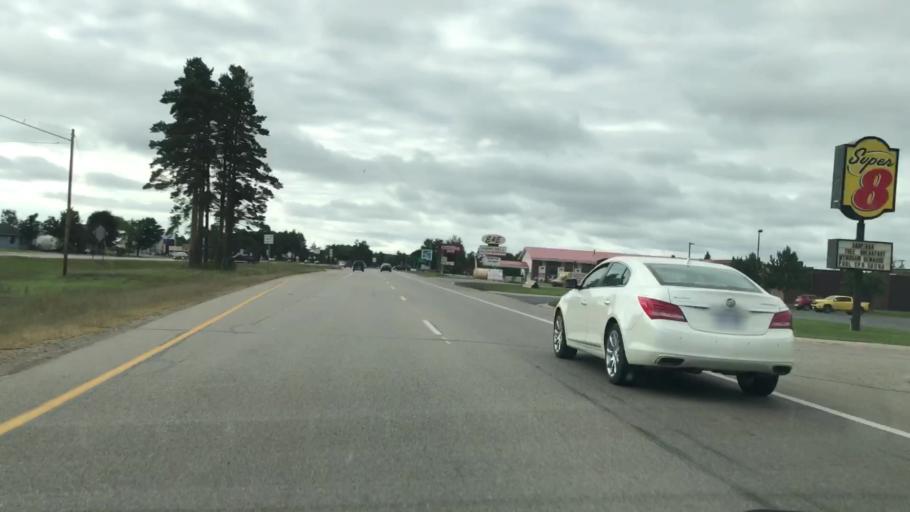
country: US
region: Michigan
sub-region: Delta County
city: Escanaba
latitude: 45.7776
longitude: -87.0833
